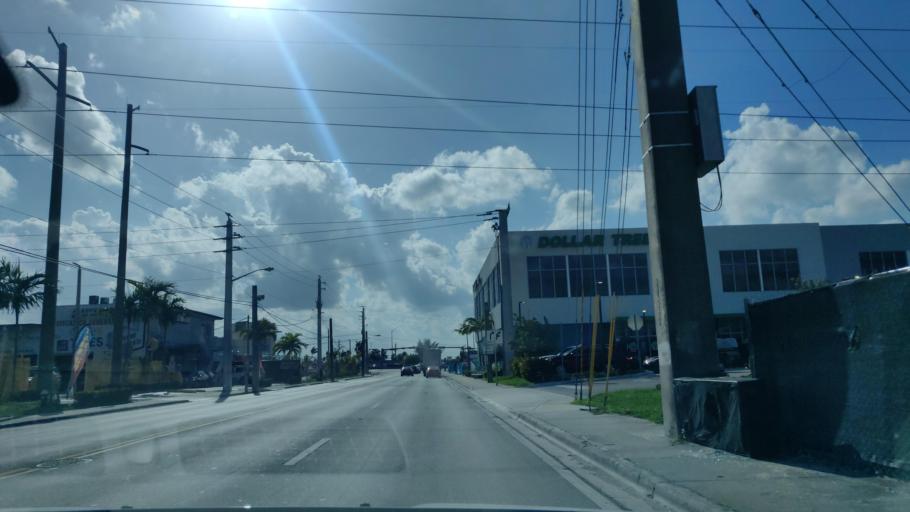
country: US
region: Florida
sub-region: Miami-Dade County
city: Hialeah Gardens
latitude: 25.8481
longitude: -80.3123
